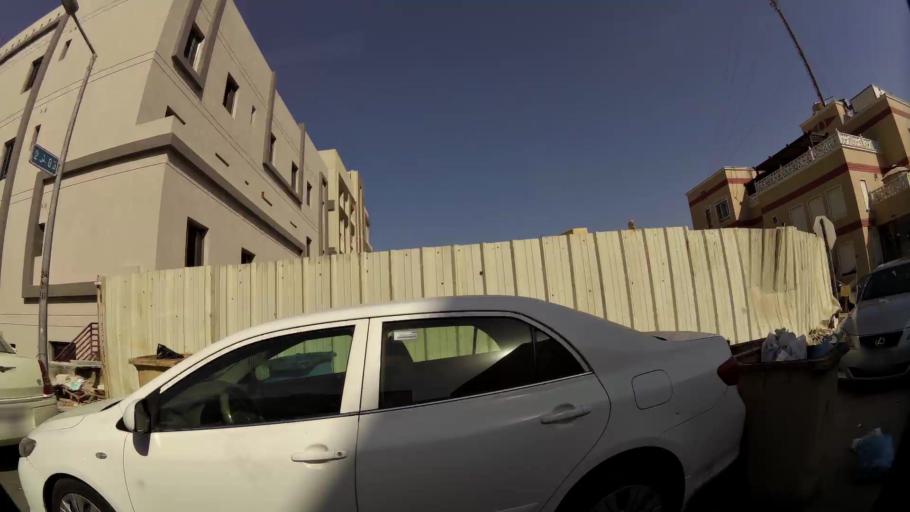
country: KW
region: Muhafazat Hawalli
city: Salwa
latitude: 29.2918
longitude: 48.0813
